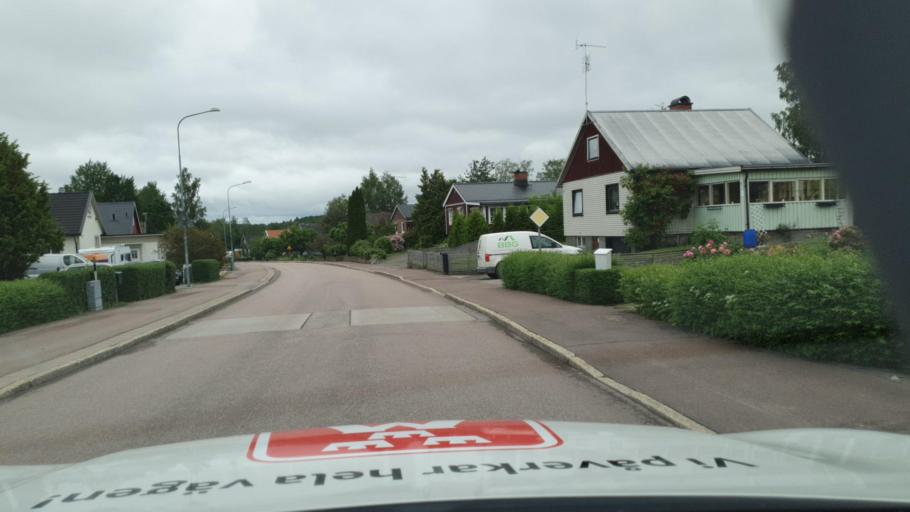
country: SE
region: Vaermland
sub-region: Grums Kommun
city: Grums
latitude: 59.3586
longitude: 13.1068
